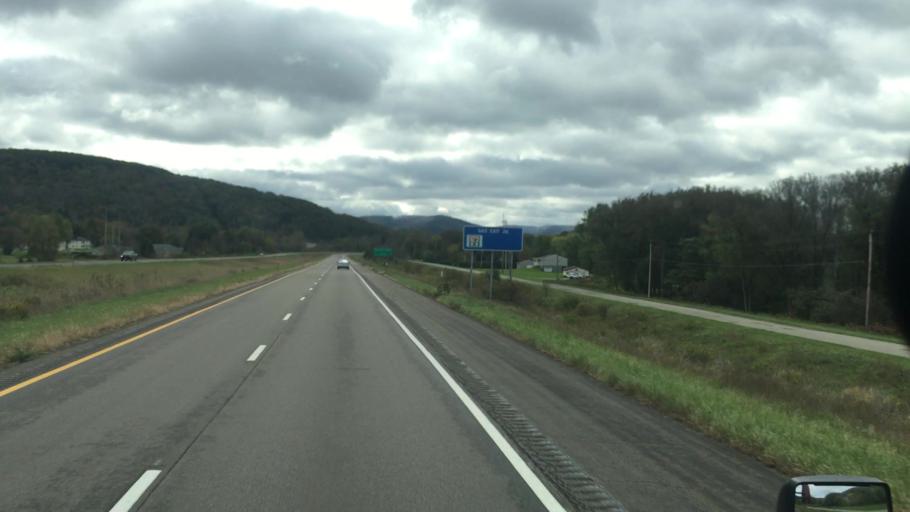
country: US
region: New York
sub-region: Cattaraugus County
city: Olean
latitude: 42.1181
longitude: -78.4181
